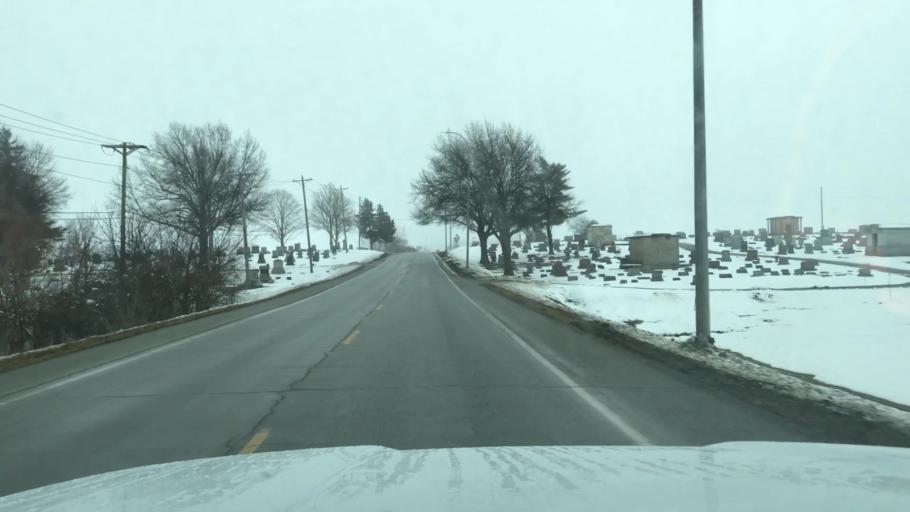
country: US
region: Missouri
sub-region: Clinton County
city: Cameron
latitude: 39.7318
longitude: -94.2270
